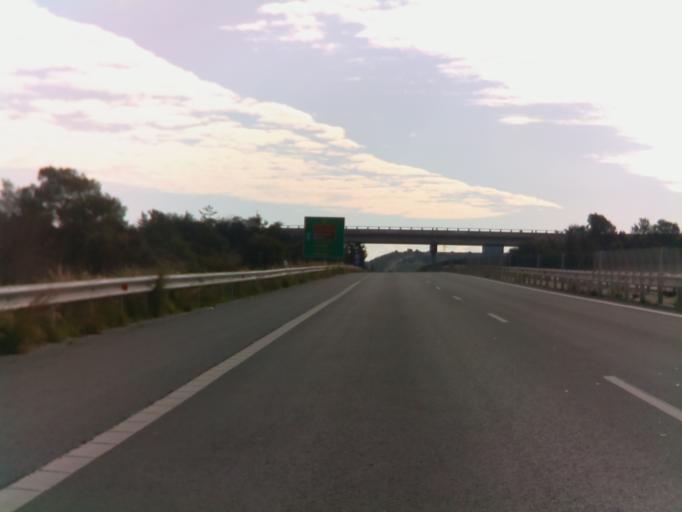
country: CY
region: Limassol
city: Pyrgos
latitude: 34.7292
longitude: 33.2376
